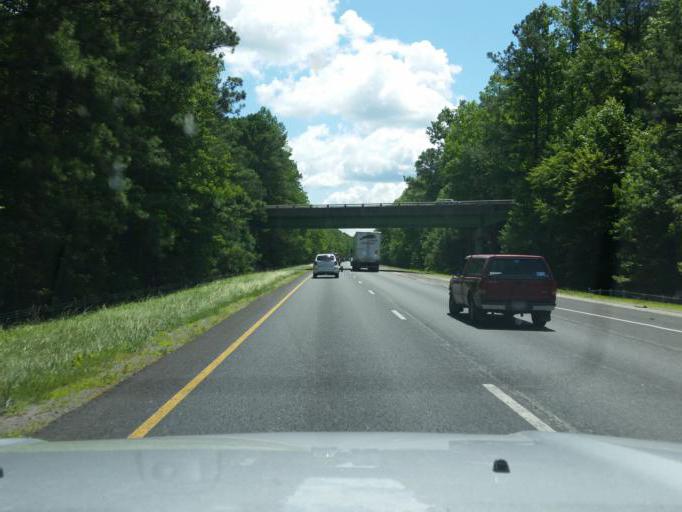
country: US
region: Virginia
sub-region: New Kent County
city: New Kent
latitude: 37.4781
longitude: -76.9194
